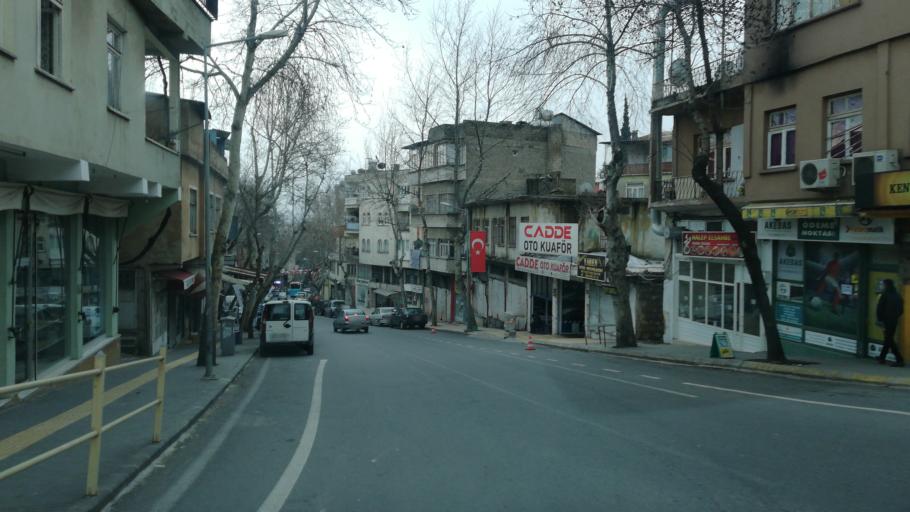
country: TR
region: Kahramanmaras
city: Kahramanmaras
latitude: 37.5899
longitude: 36.9269
